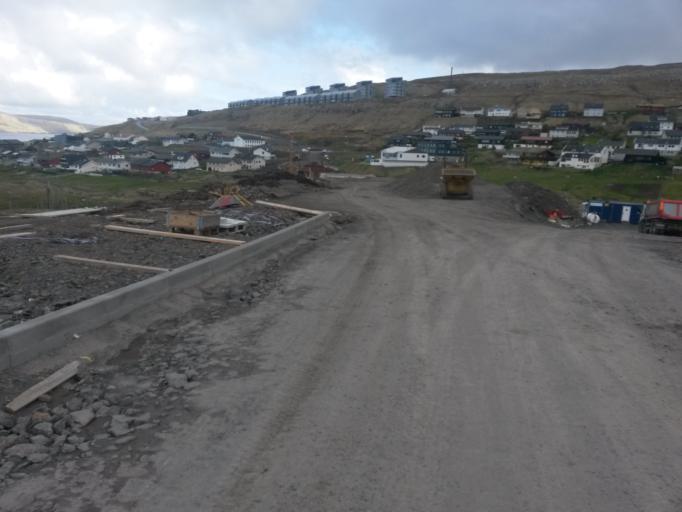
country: FO
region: Streymoy
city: Argir
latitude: 61.9988
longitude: -6.7952
